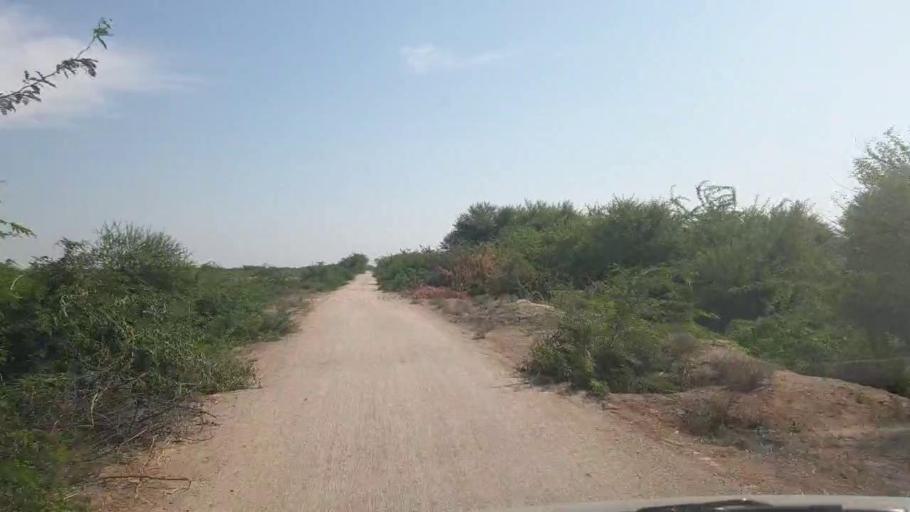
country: PK
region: Sindh
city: Digri
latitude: 24.9569
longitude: 69.1361
